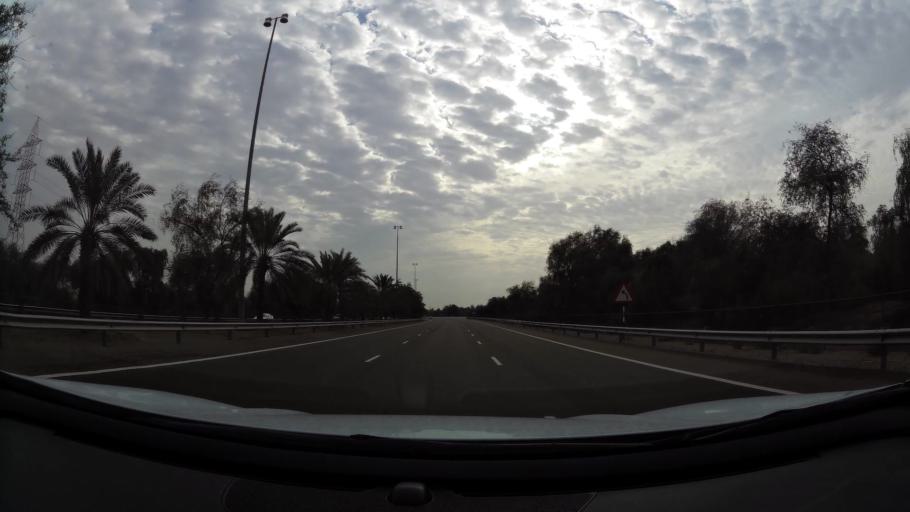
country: AE
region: Abu Dhabi
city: Al Ain
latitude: 24.1710
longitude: 55.2199
